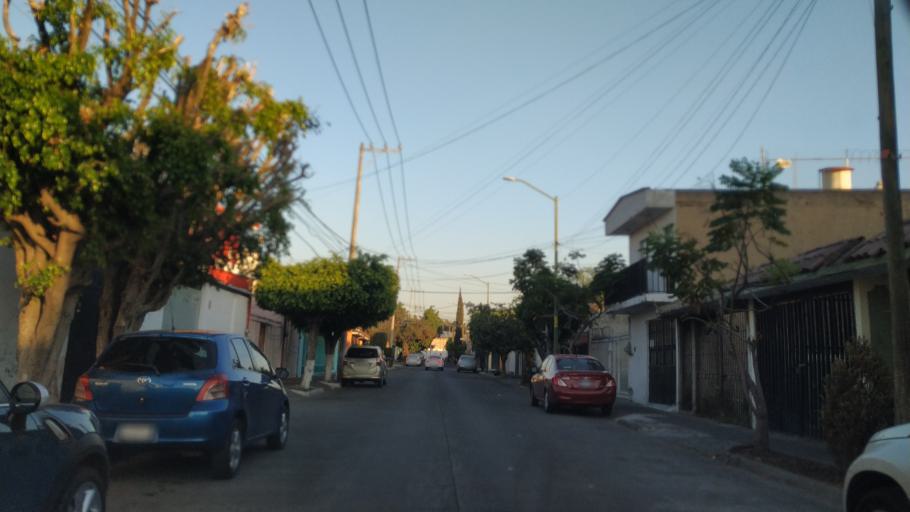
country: MX
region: Jalisco
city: Tlaquepaque
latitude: 20.6519
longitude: -103.3330
